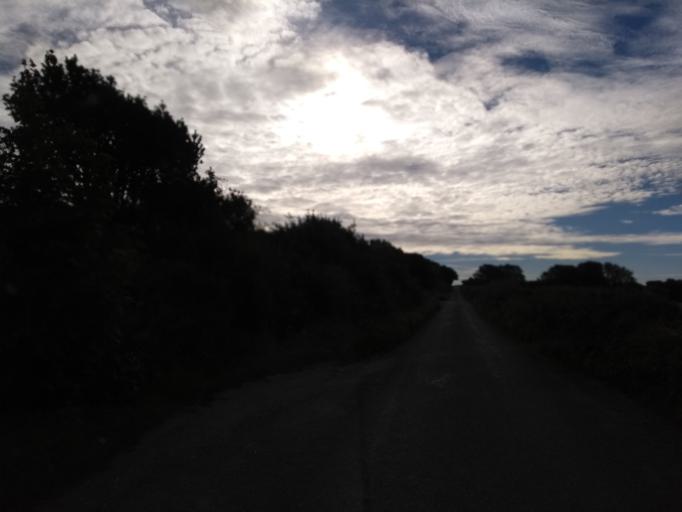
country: GB
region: England
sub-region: Dorset
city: Beaminster
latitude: 50.8283
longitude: -2.7279
